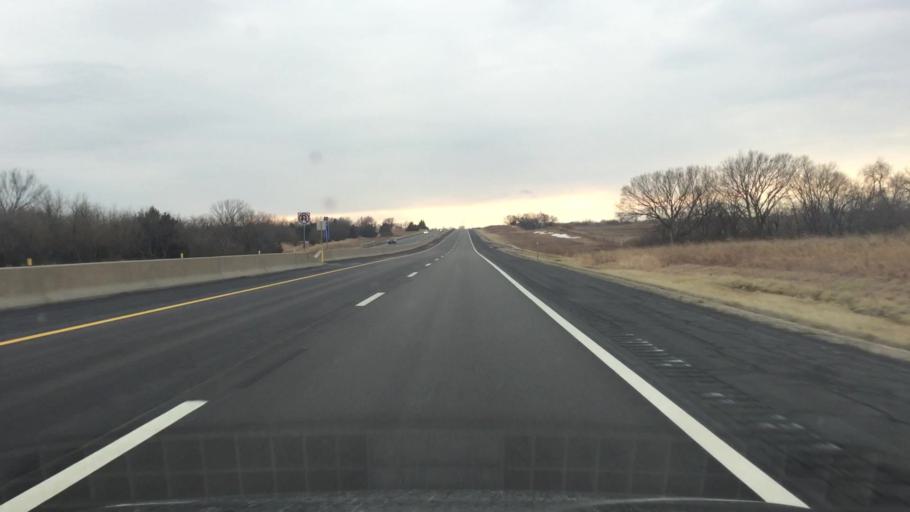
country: US
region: Kansas
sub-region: Shawnee County
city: Auburn
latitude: 38.8380
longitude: -95.8744
